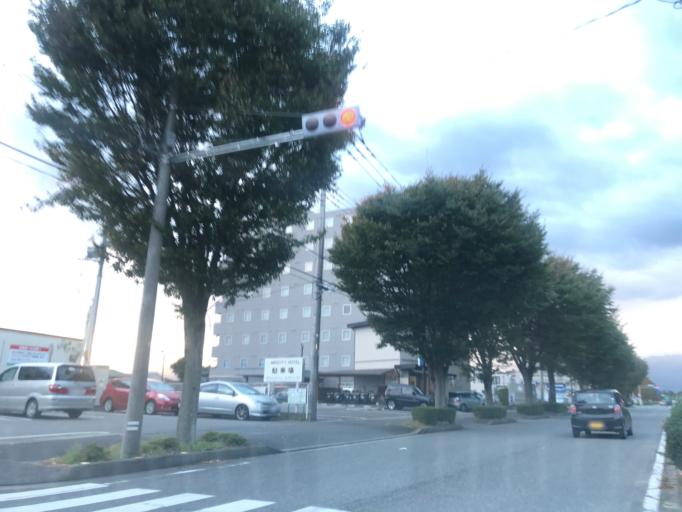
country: JP
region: Tochigi
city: Kuroiso
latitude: 36.9331
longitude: 140.0187
